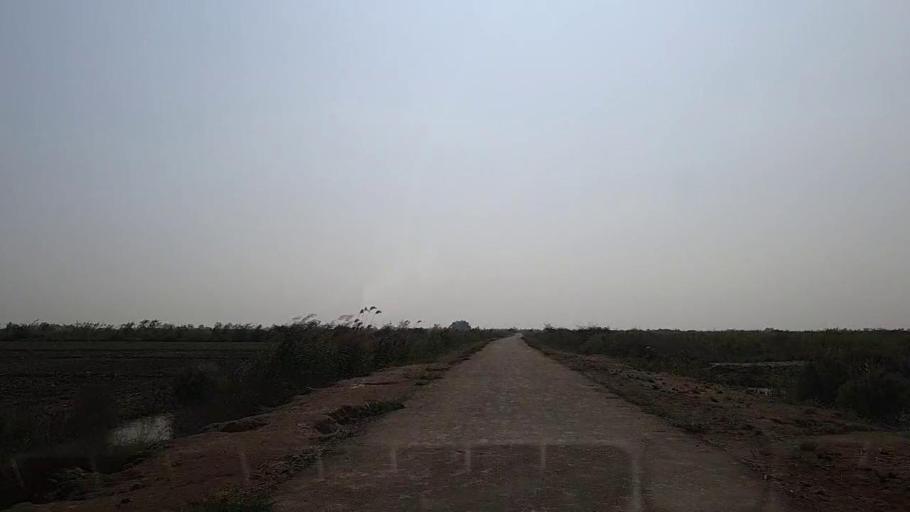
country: PK
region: Sindh
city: Mirpur Sakro
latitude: 24.6567
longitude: 67.6918
